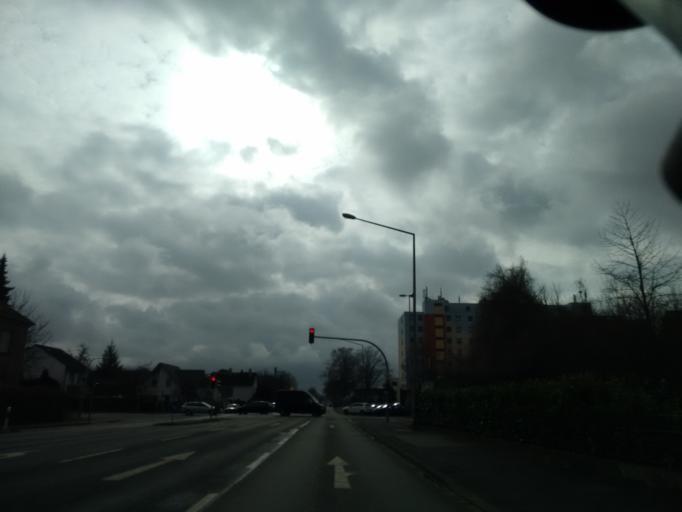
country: DE
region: North Rhine-Westphalia
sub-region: Regierungsbezirk Detmold
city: Paderborn
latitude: 51.7385
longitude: 8.7692
